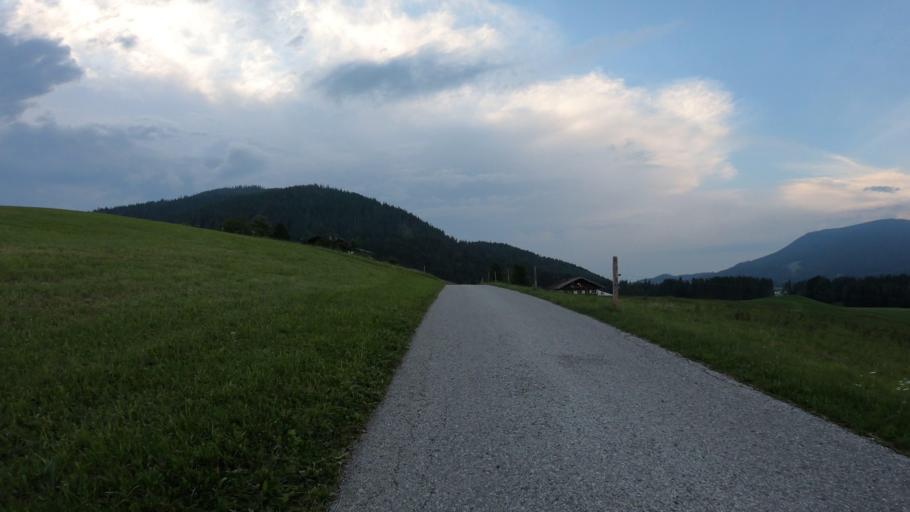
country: DE
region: Bavaria
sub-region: Upper Bavaria
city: Inzell
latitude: 47.7632
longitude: 12.7240
